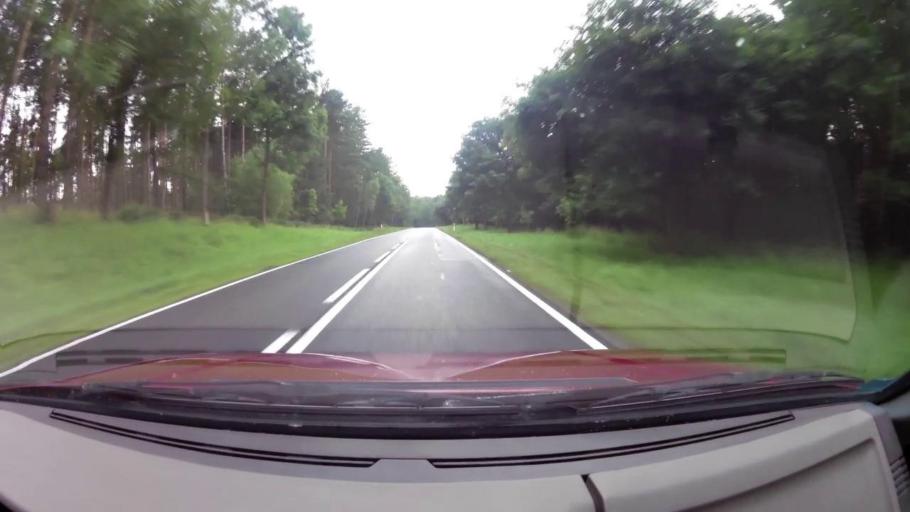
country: PL
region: West Pomeranian Voivodeship
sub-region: Powiat lobeski
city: Wegorzyno
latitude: 53.5276
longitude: 15.5259
